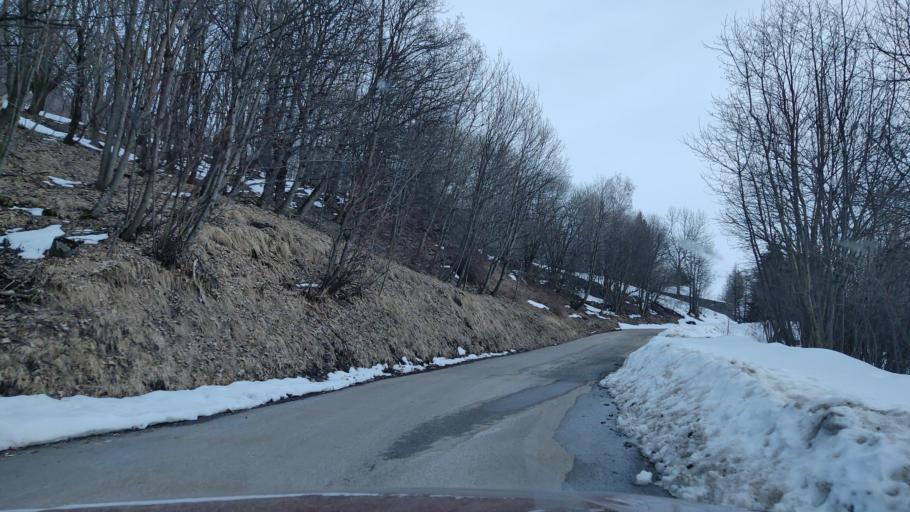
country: FR
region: Rhone-Alpes
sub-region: Departement de la Savoie
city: Saint-Michel-de-Maurienne
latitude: 45.2445
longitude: 6.4764
